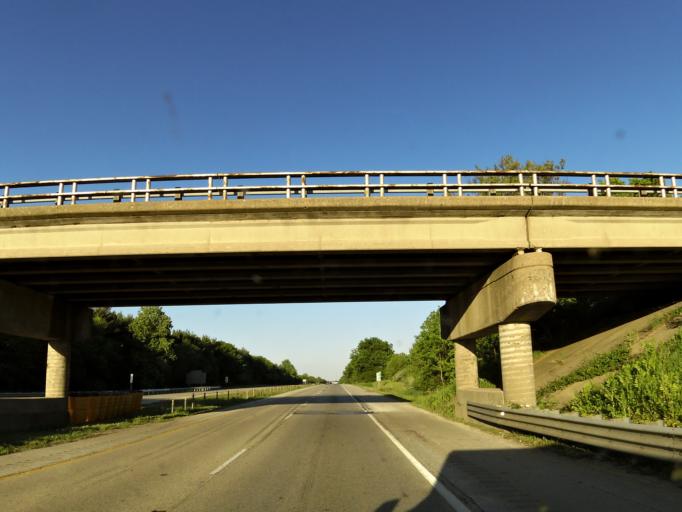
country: US
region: Illinois
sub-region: Champaign County
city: Urbana
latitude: 40.1202
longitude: -88.1630
